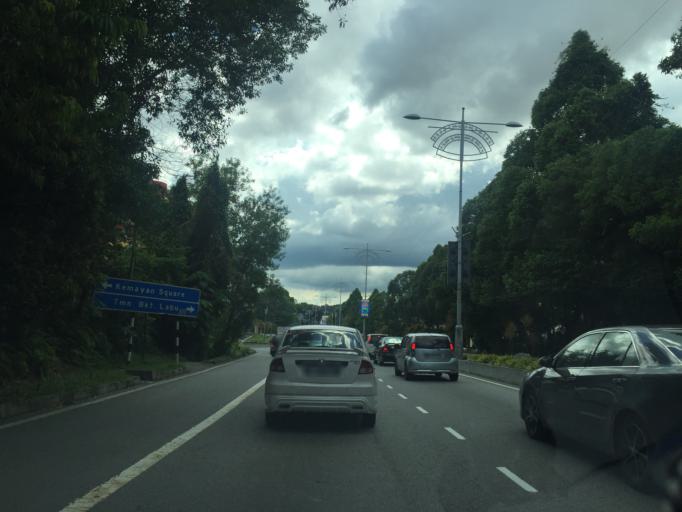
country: MY
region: Negeri Sembilan
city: Seremban
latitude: 2.7216
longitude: 101.9229
